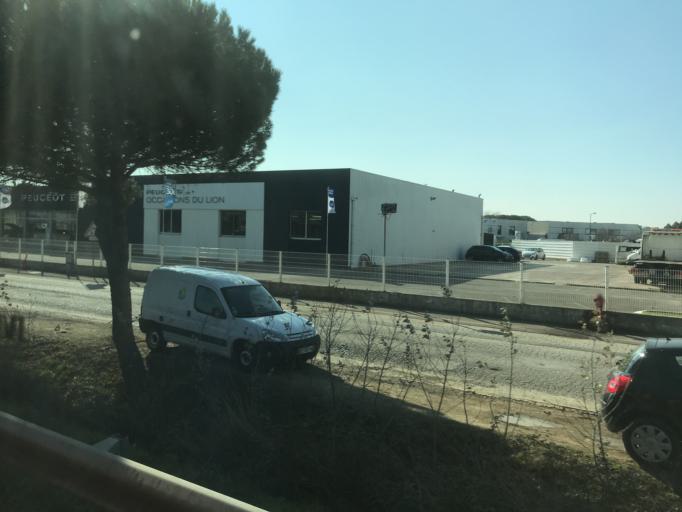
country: FR
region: Languedoc-Roussillon
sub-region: Departement de l'Herault
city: Perols
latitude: 43.5883
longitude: 3.9401
